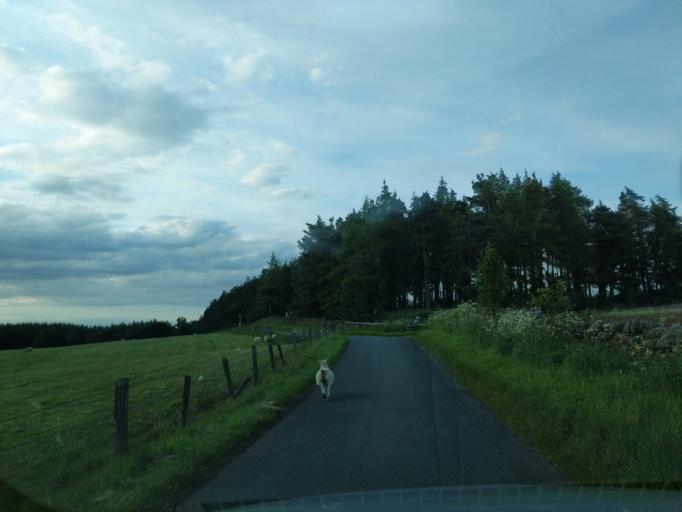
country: GB
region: Scotland
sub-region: Midlothian
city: Gorebridge
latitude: 55.7835
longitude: -3.0970
